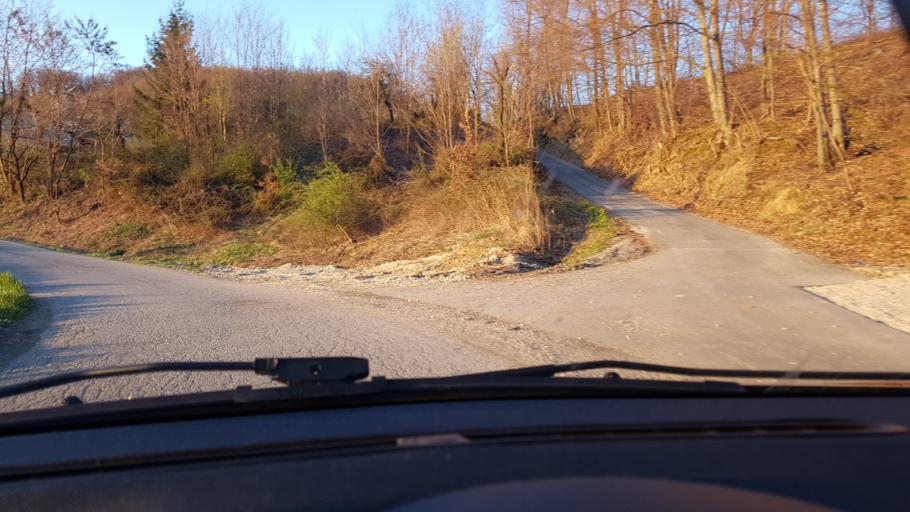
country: SI
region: Rogatec
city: Rogatec
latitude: 46.1781
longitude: 15.6828
